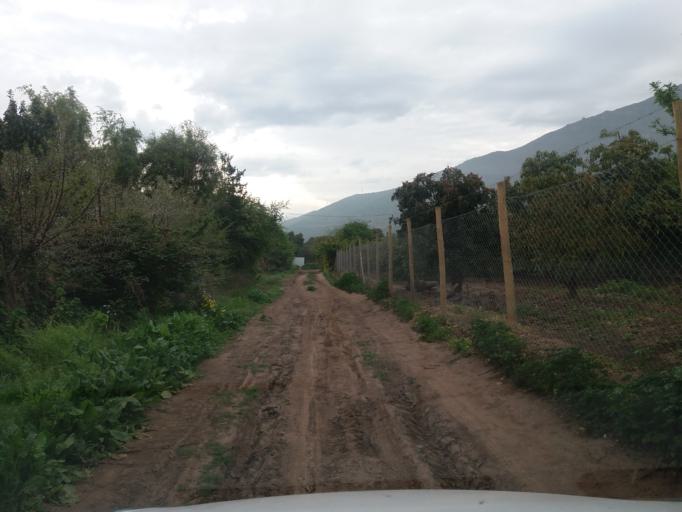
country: CL
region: Valparaiso
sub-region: Provincia de San Felipe
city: Llaillay
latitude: -32.8478
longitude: -71.0586
